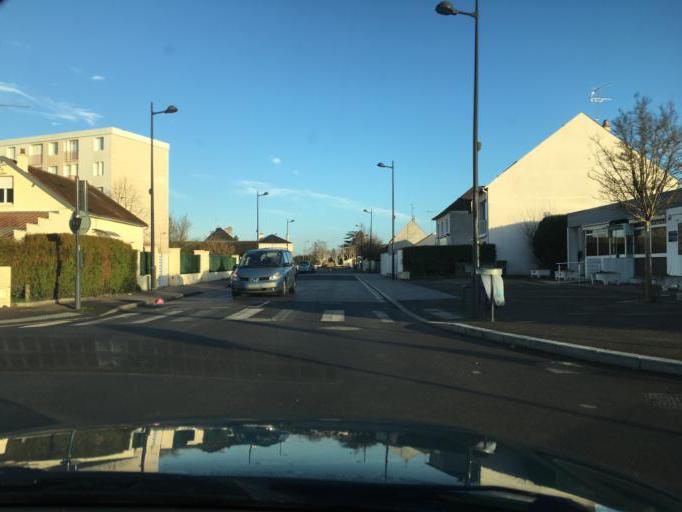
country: FR
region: Centre
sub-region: Departement du Loiret
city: Saint-Jean-de-Braye
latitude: 47.9091
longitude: 1.9536
